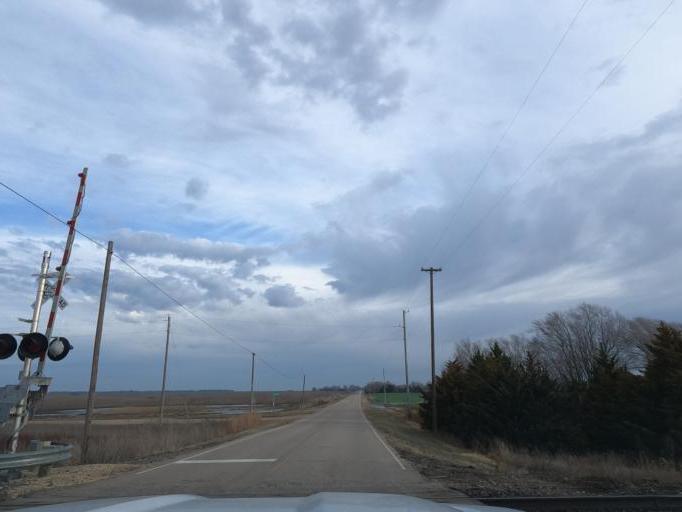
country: US
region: Kansas
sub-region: Reno County
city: South Hutchinson
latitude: 37.9699
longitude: -98.0876
